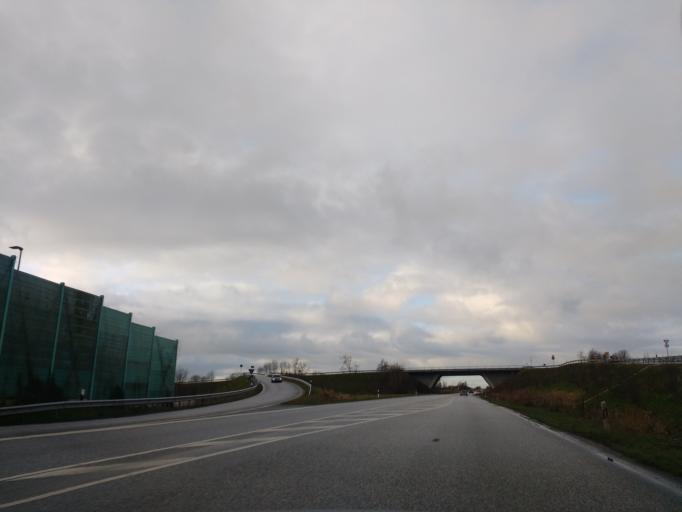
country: DE
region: Schleswig-Holstein
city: Heiligenstedten
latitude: 53.9355
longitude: 9.4728
